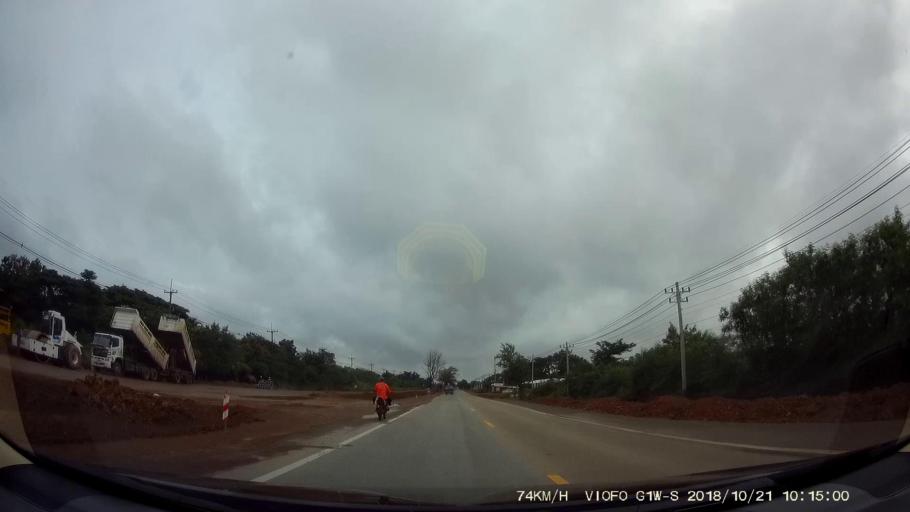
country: TH
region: Chaiyaphum
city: Phu Khiao
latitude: 16.3445
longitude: 102.1614
